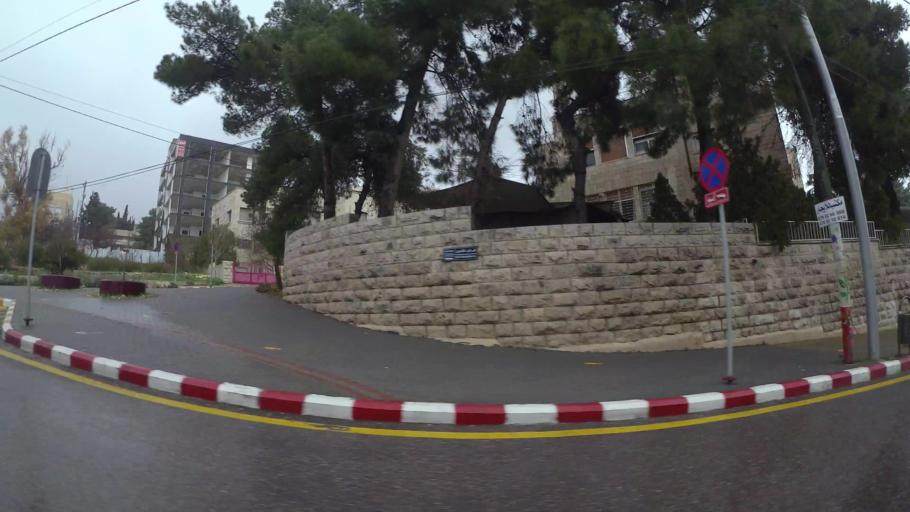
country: JO
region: Amman
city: Amman
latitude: 31.9536
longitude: 35.8991
